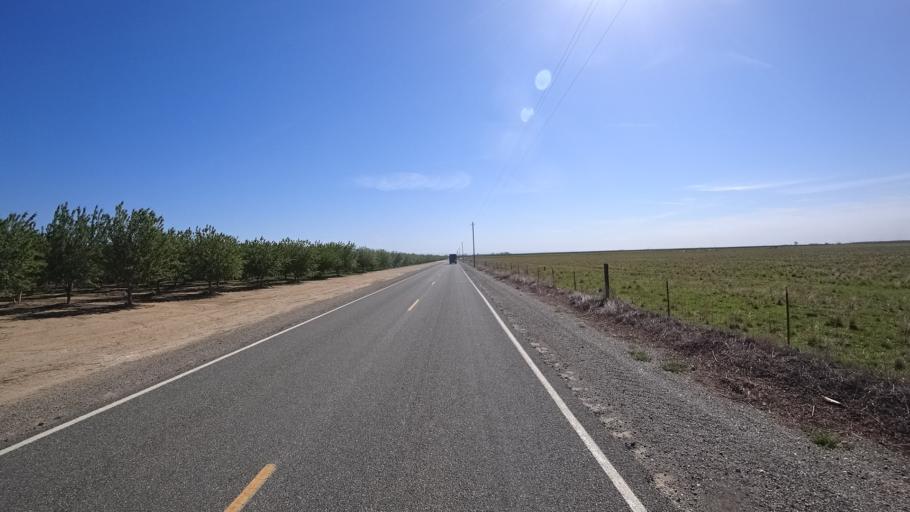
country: US
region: California
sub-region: Glenn County
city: Willows
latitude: 39.6238
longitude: -122.1496
